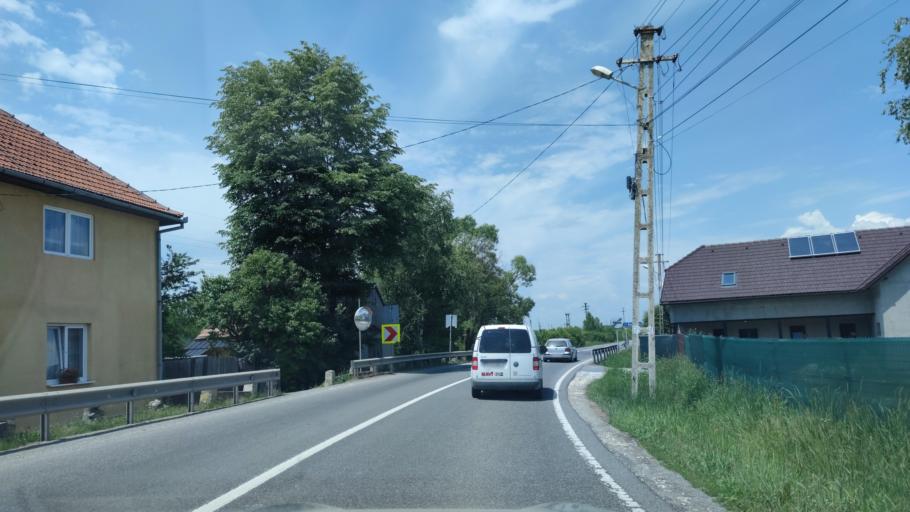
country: RO
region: Harghita
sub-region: Comuna Voslobeni
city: Voslobeni
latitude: 46.6284
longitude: 25.6260
